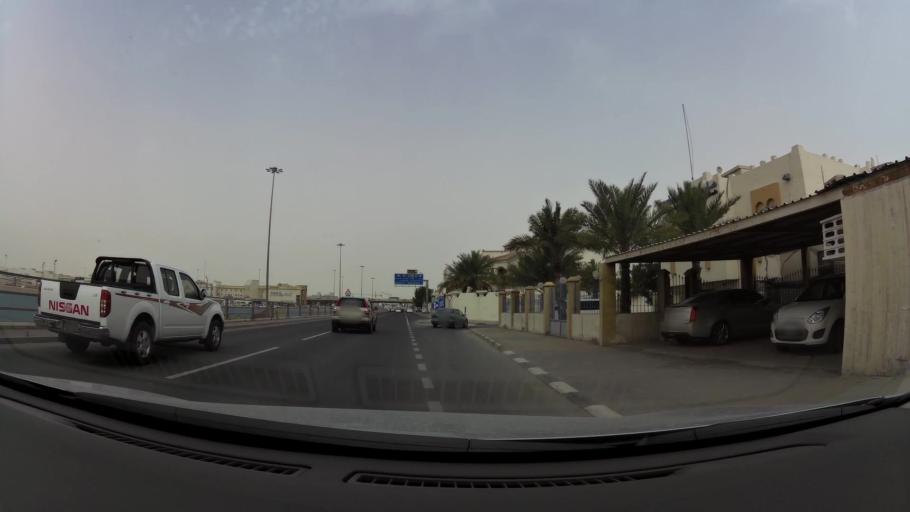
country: QA
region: Baladiyat ad Dawhah
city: Doha
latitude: 25.2611
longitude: 51.4992
